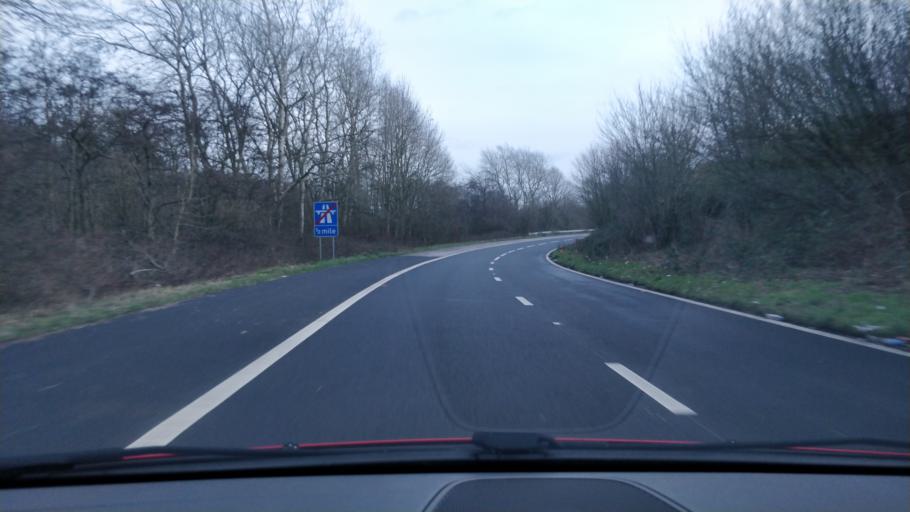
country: GB
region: England
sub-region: Knowsley
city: Knowsley
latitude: 53.4369
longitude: -2.8545
